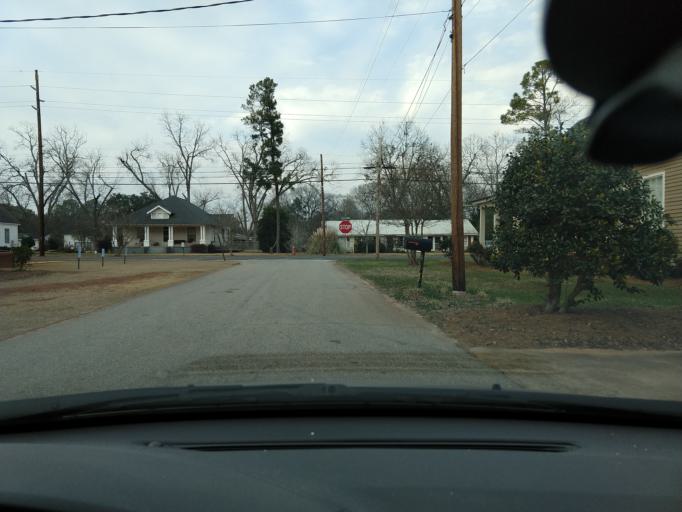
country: US
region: Georgia
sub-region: Webster County
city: Preston
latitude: 32.0336
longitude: -84.3975
